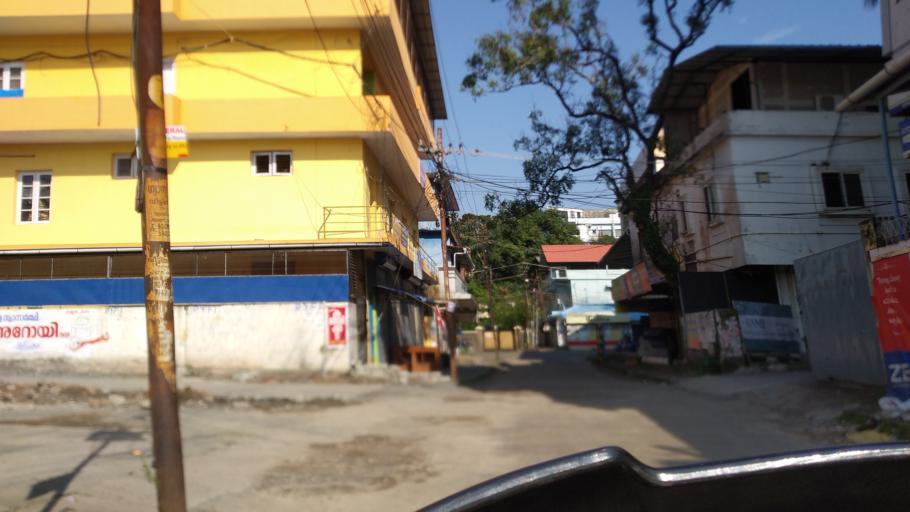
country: IN
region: Kerala
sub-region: Ernakulam
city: Cochin
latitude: 9.9828
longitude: 76.2801
